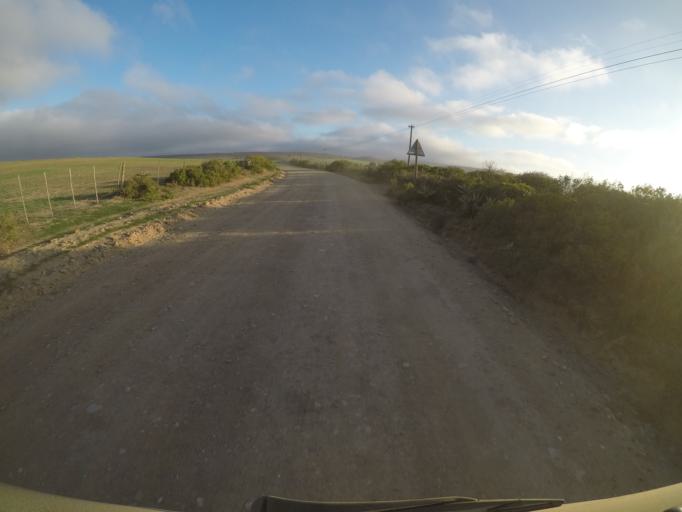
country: ZA
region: Western Cape
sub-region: Eden District Municipality
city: Mossel Bay
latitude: -34.1127
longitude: 22.0534
